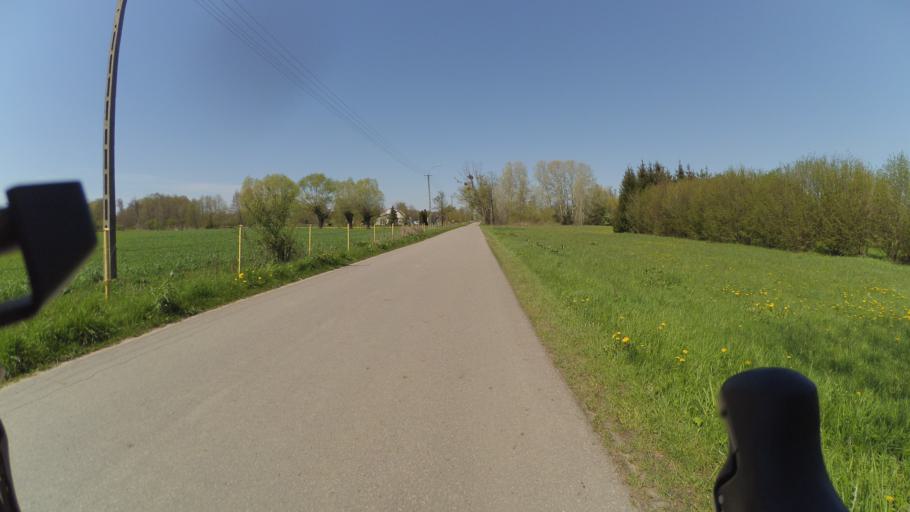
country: PL
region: Masovian Voivodeship
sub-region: Powiat nowodworski
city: Zakroczym
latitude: 52.4136
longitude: 20.5282
